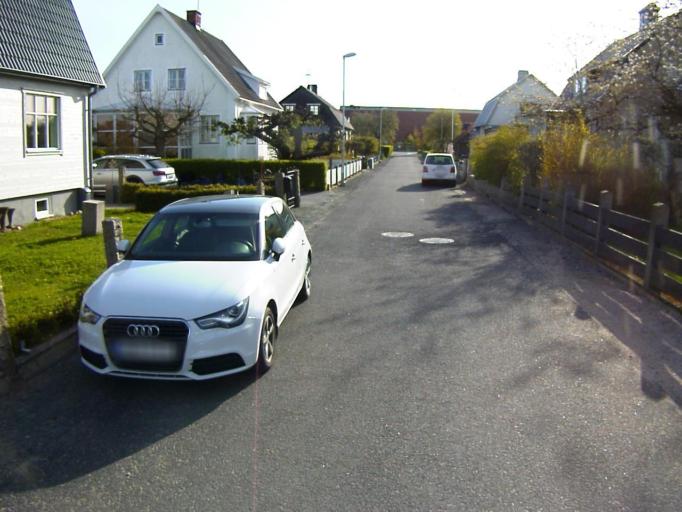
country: SE
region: Skane
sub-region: Kristianstads Kommun
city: Kristianstad
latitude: 56.0145
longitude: 14.1490
